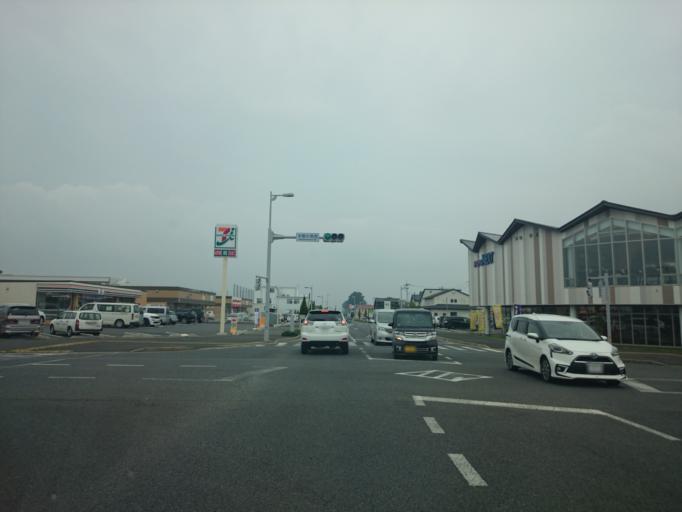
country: JP
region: Ibaraki
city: Naka
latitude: 36.0989
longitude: 140.0761
